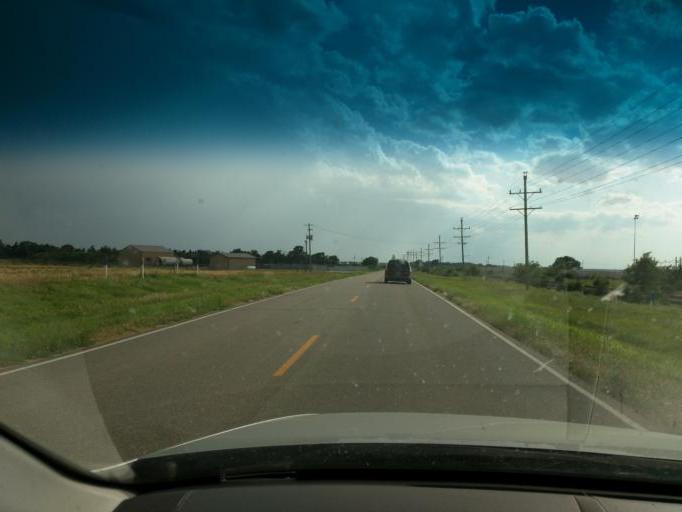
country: US
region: Kansas
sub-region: Reno County
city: South Hutchinson
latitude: 38.0207
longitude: -97.9900
